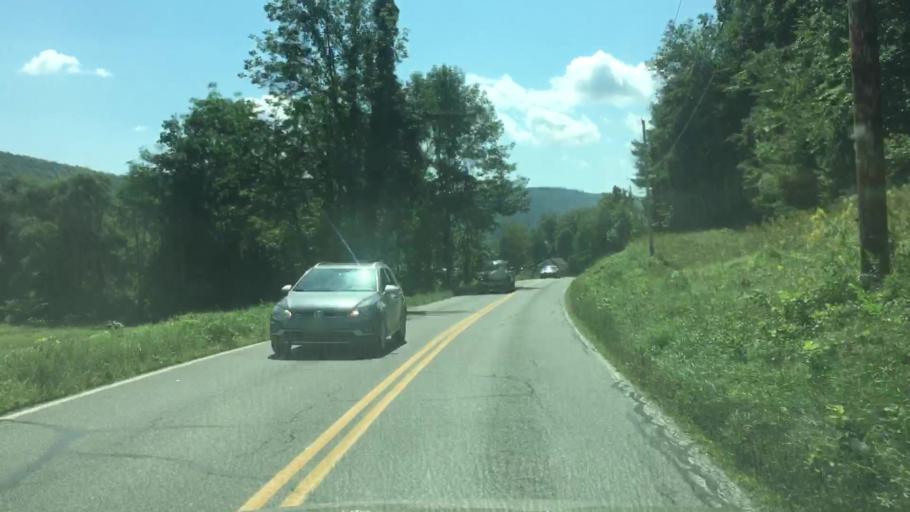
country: US
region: Vermont
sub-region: Windham County
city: West Brattleboro
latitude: 42.7986
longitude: -72.5987
